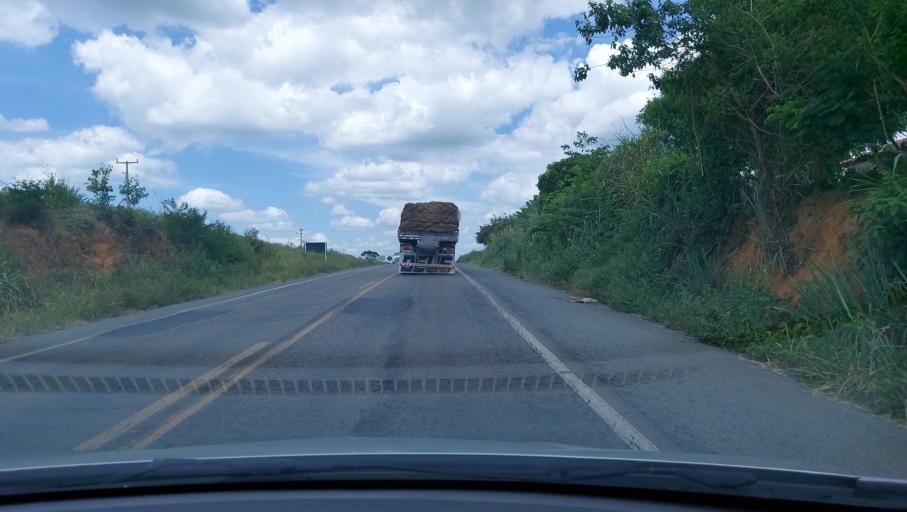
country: BR
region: Bahia
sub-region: Ruy Barbosa
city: Terra Nova
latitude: -12.4433
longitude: -40.7859
